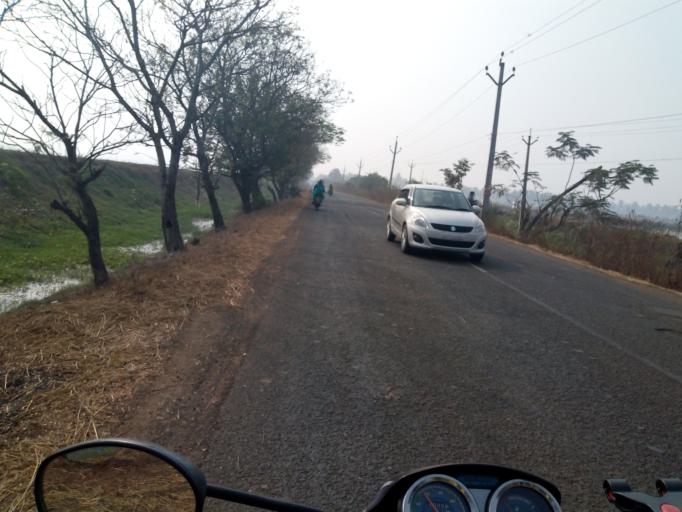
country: IN
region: Andhra Pradesh
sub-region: West Godavari
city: Tadepallegudem
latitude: 16.7907
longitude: 81.4189
